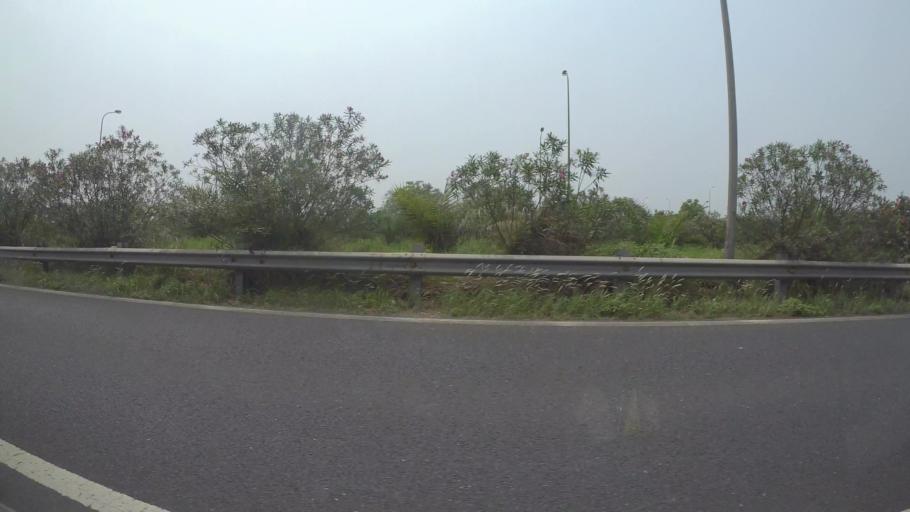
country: VN
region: Ha Noi
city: Quoc Oai
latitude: 21.0022
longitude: 105.6251
